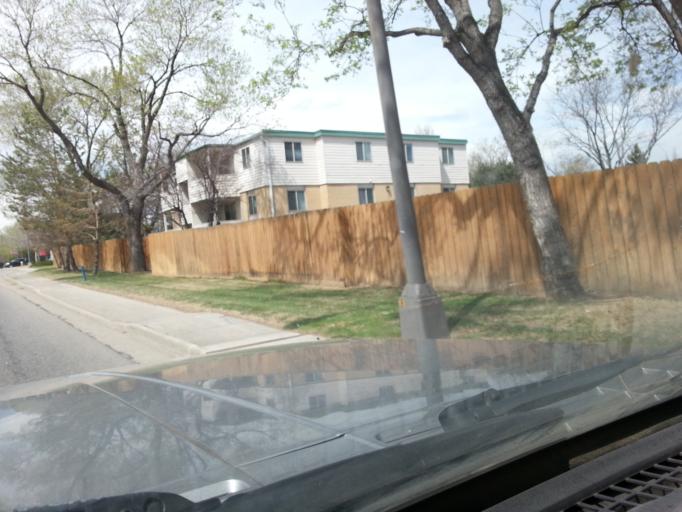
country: US
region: Colorado
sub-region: Larimer County
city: Loveland
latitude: 40.4073
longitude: -105.1065
